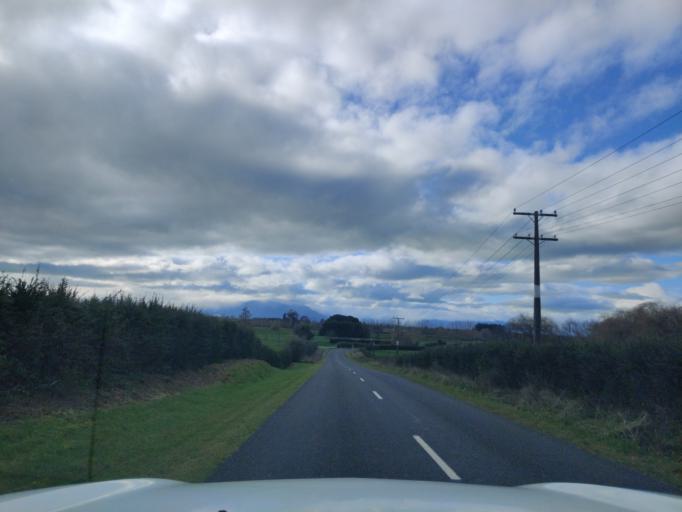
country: NZ
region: Waikato
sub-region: Hauraki District
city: Paeroa
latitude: -37.5888
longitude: 175.5110
